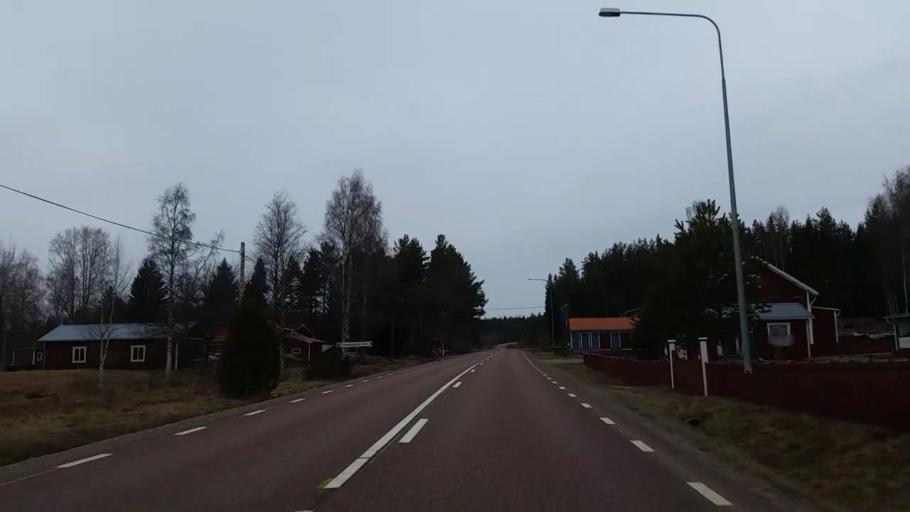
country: SE
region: Gaevleborg
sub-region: Ovanakers Kommun
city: Edsbyn
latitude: 61.2055
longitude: 15.8714
